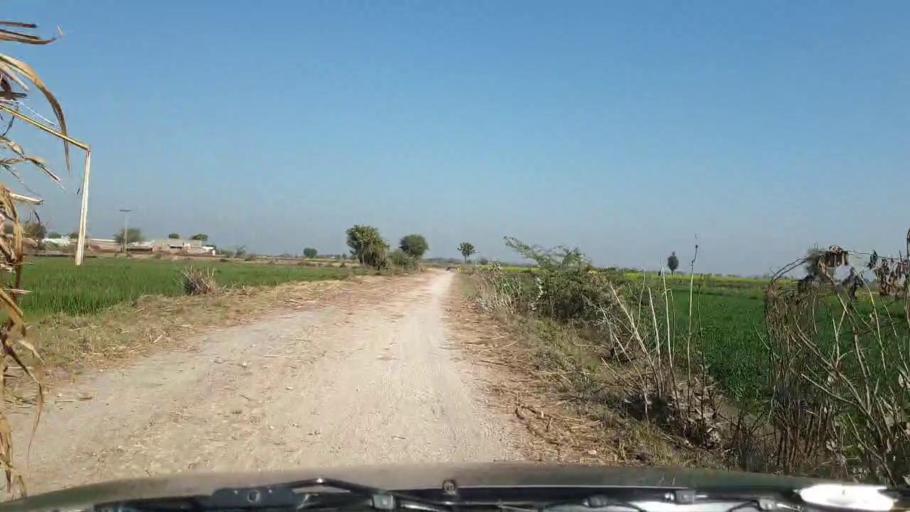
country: PK
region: Sindh
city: Jhol
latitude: 25.9626
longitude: 68.8234
